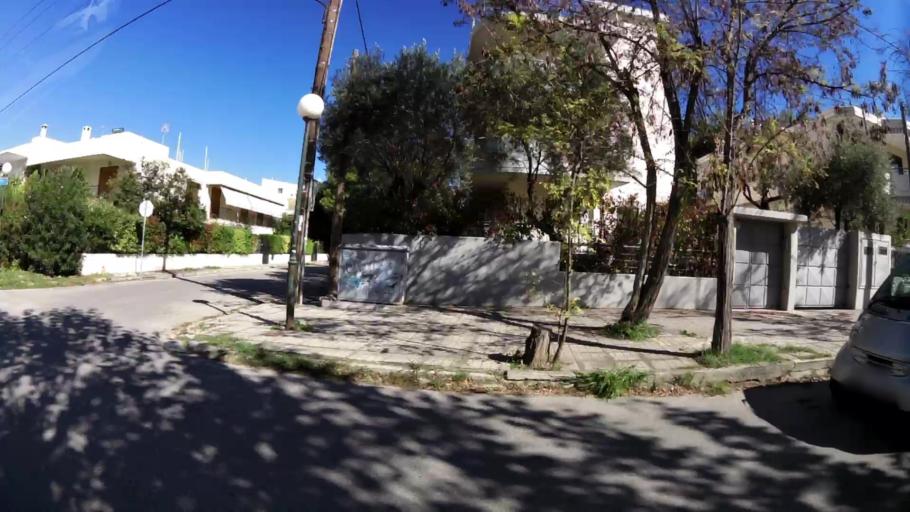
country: GR
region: Attica
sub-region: Nomarchia Athinas
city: Nea Erythraia
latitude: 38.0969
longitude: 23.7918
